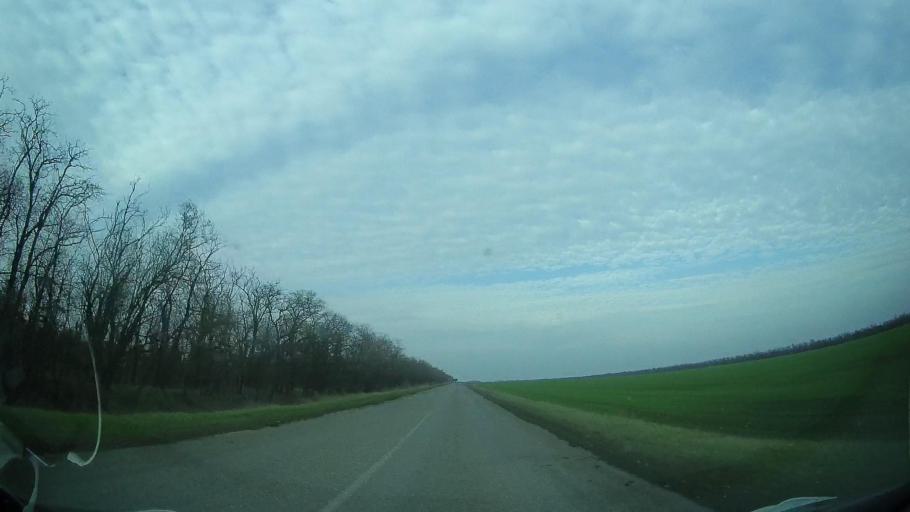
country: RU
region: Rostov
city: Zernograd
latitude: 46.9401
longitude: 40.3666
